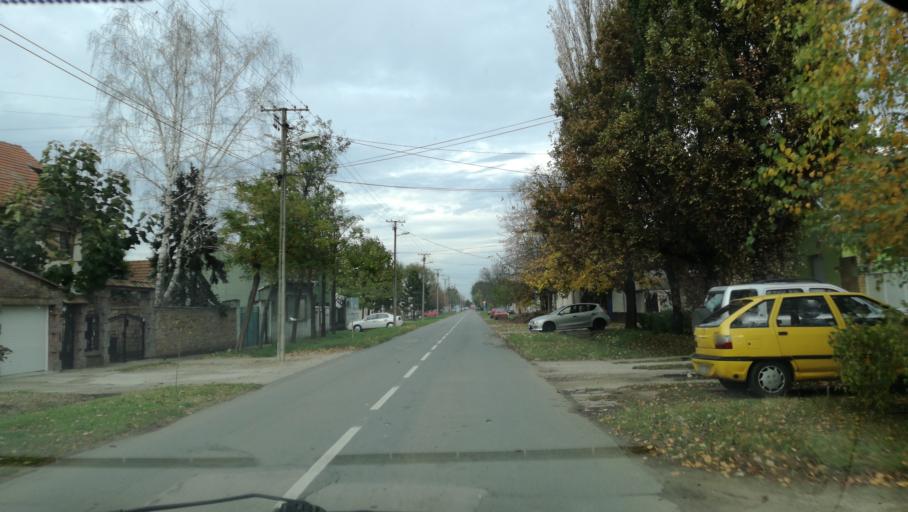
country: RS
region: Autonomna Pokrajina Vojvodina
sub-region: Severnobanatski Okrug
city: Kikinda
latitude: 45.8400
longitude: 20.4762
